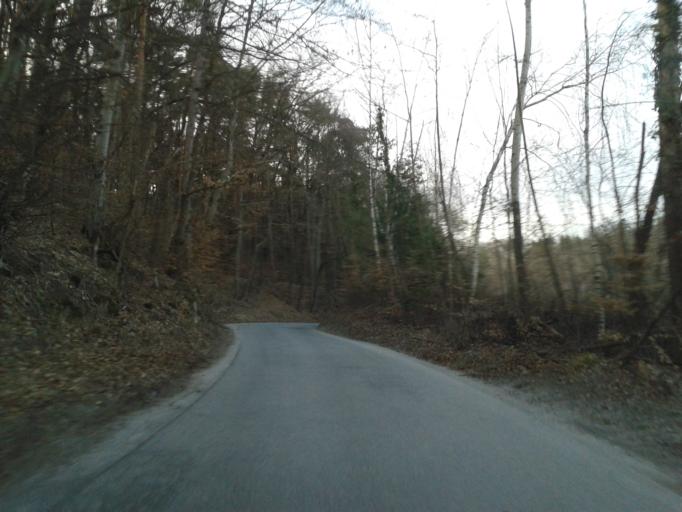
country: AT
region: Styria
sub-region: Politischer Bezirk Graz-Umgebung
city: Stattegg
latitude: 47.1351
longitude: 15.4388
